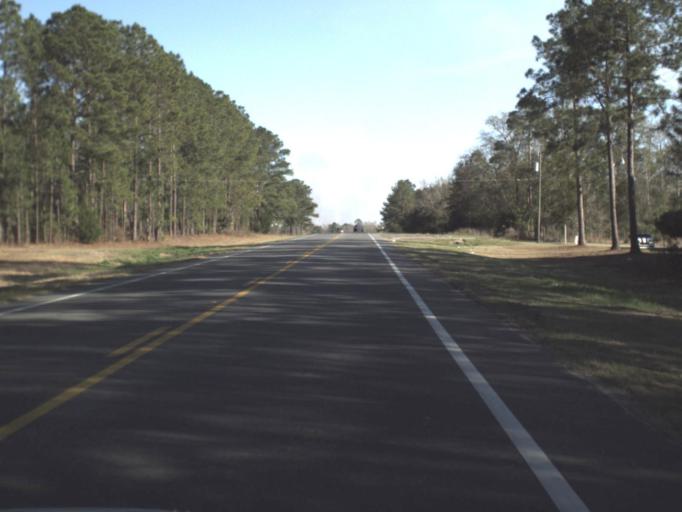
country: US
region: Florida
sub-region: Jackson County
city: Marianna
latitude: 30.7258
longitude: -85.0841
